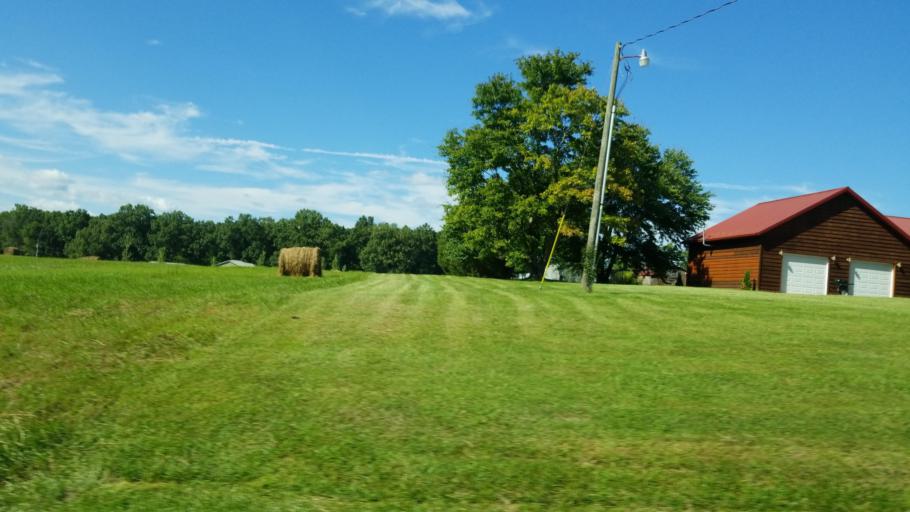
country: US
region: Illinois
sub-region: Saline County
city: Carrier Mills
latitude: 37.7990
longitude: -88.7150
